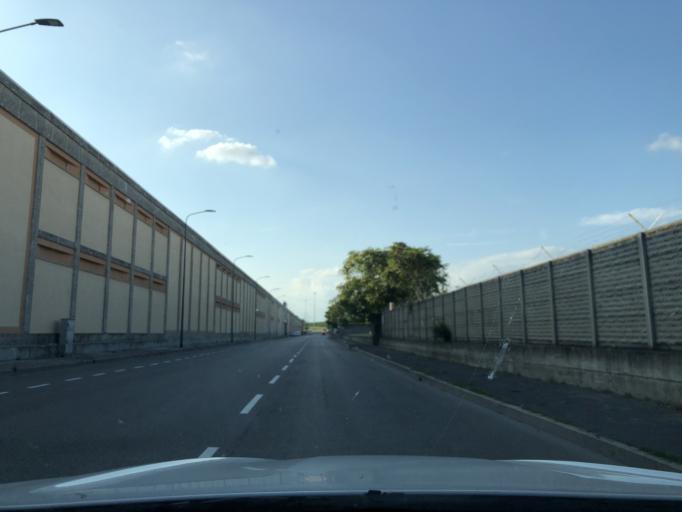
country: IT
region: Lombardy
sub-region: Citta metropolitana di Milano
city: Baranzate
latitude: 45.5089
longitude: 9.1171
